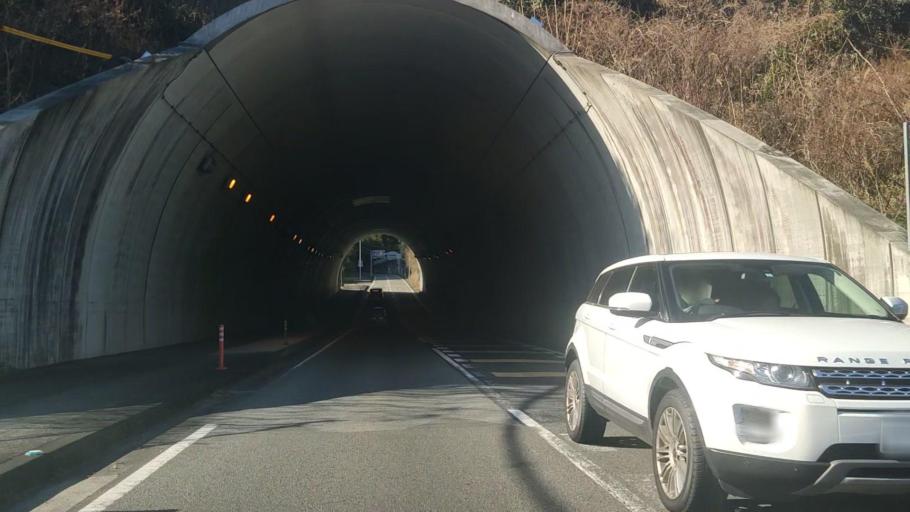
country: JP
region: Oita
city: Saiki
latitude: 32.9740
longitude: 131.8637
